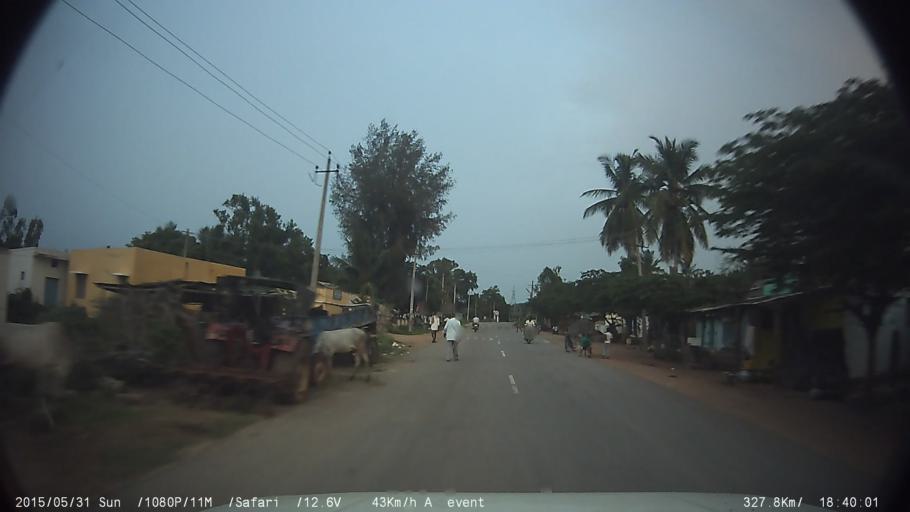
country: IN
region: Karnataka
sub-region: Mysore
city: Nanjangud
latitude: 12.1482
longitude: 76.7844
